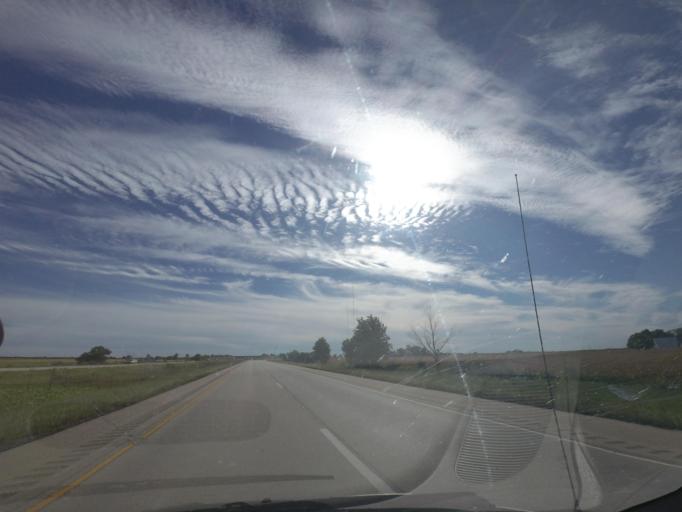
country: US
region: Illinois
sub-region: Piatt County
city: Cerro Gordo
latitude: 39.9620
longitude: -88.8175
